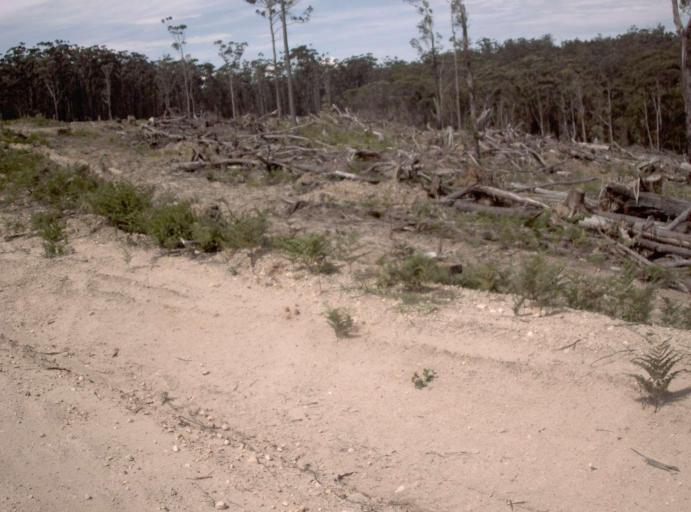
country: AU
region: Victoria
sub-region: East Gippsland
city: Lakes Entrance
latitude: -37.6390
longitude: 148.6629
